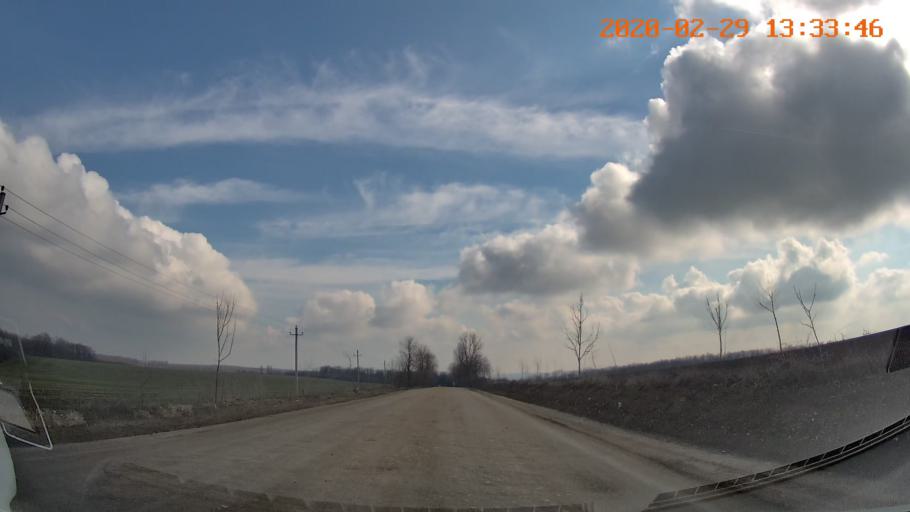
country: MD
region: Telenesti
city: Camenca
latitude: 47.8720
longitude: 28.6186
